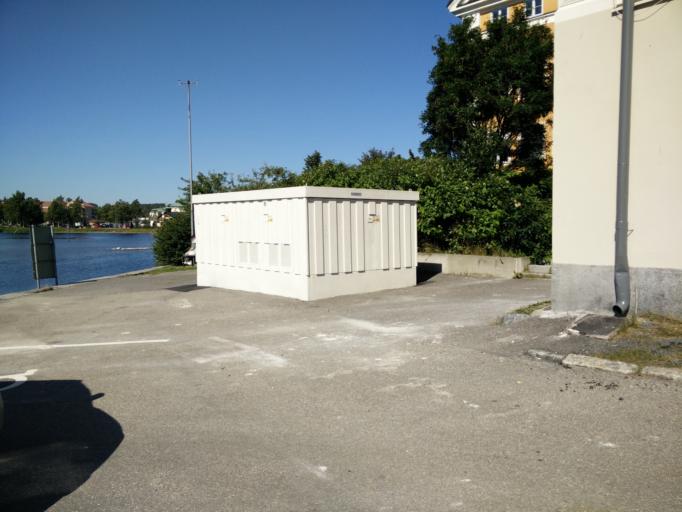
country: SE
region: Vaesternorrland
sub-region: Haernoesands Kommun
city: Haernoesand
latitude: 62.6319
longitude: 17.9372
